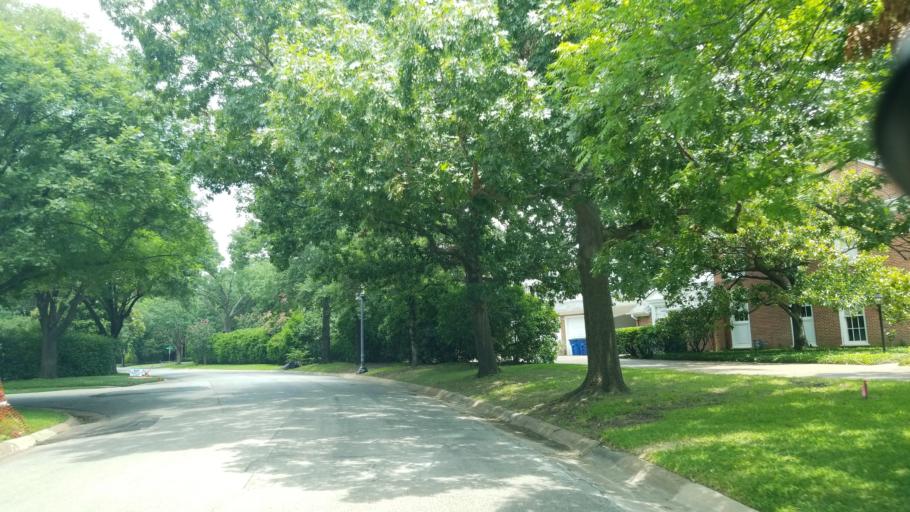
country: US
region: Texas
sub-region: Dallas County
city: University Park
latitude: 32.8429
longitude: -96.8167
